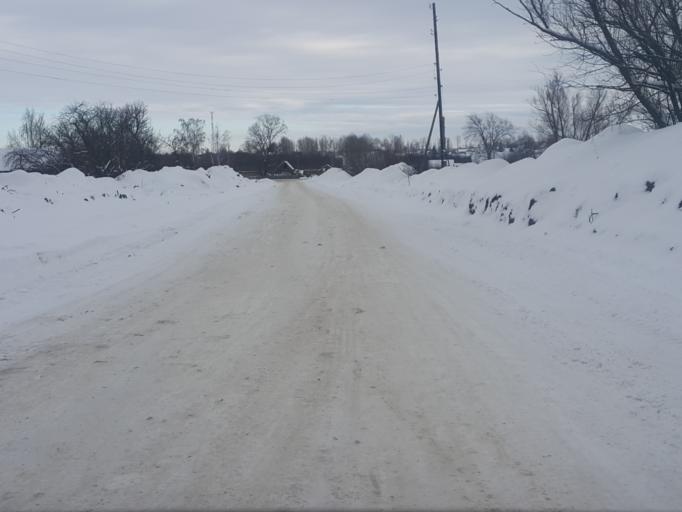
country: RU
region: Tambov
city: Platonovka
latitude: 52.8808
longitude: 41.8741
